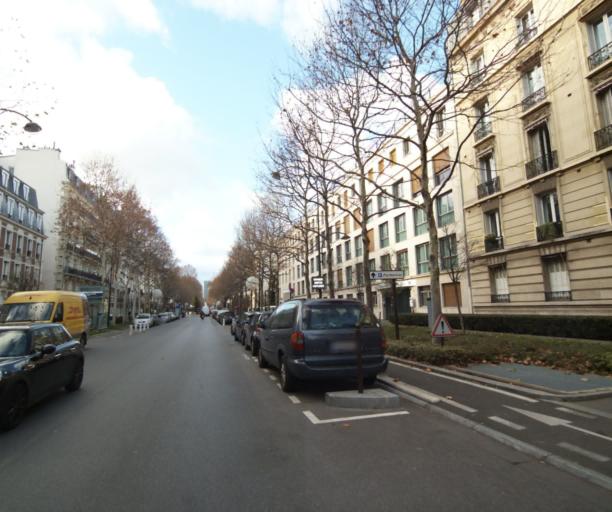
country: FR
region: Ile-de-France
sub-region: Departement des Hauts-de-Seine
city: Neuilly-sur-Seine
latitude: 48.8822
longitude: 2.2791
